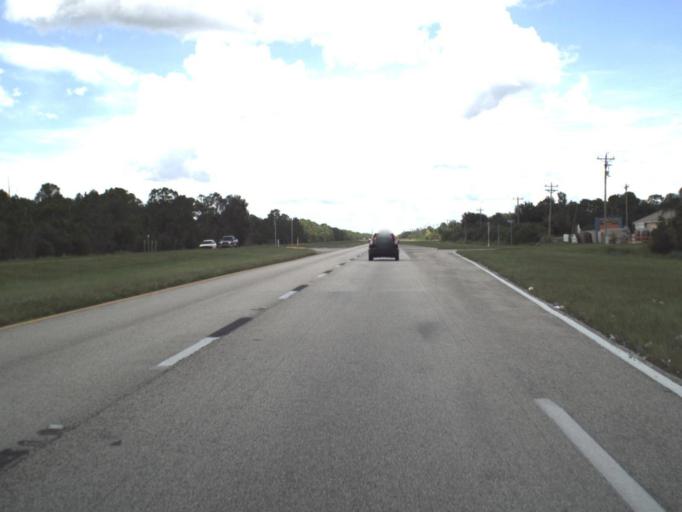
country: US
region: Florida
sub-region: Lee County
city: Burnt Store Marina
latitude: 26.7912
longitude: -81.9447
